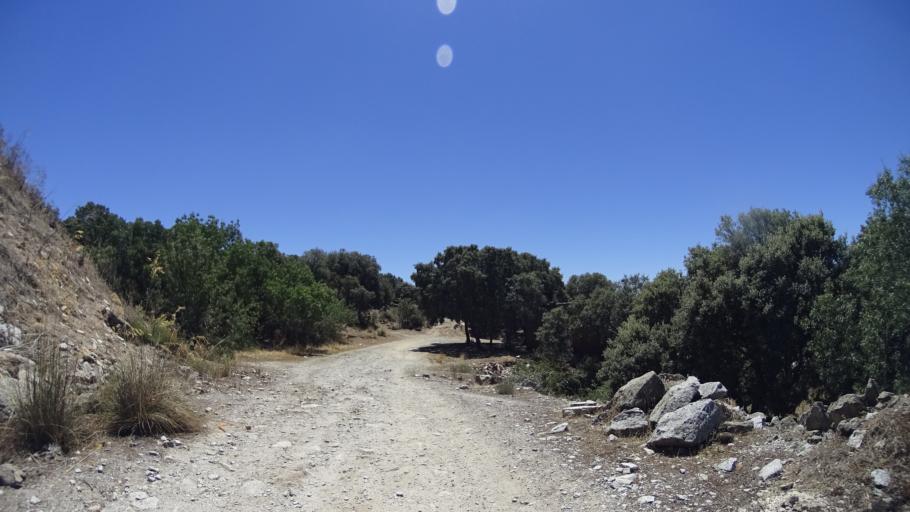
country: ES
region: Madrid
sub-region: Provincia de Madrid
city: Alpedrete
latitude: 40.6750
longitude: -4.0190
